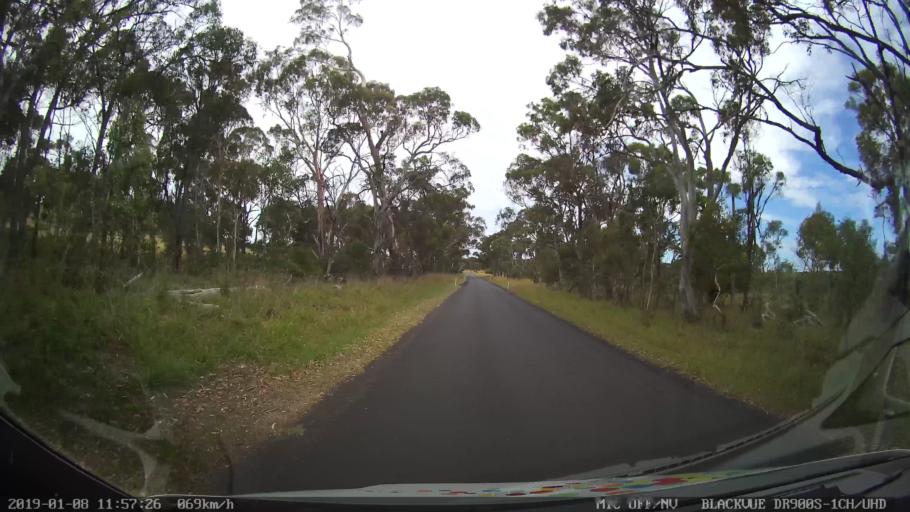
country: AU
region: New South Wales
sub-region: Armidale Dumaresq
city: Armidale
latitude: -30.4499
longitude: 151.5670
